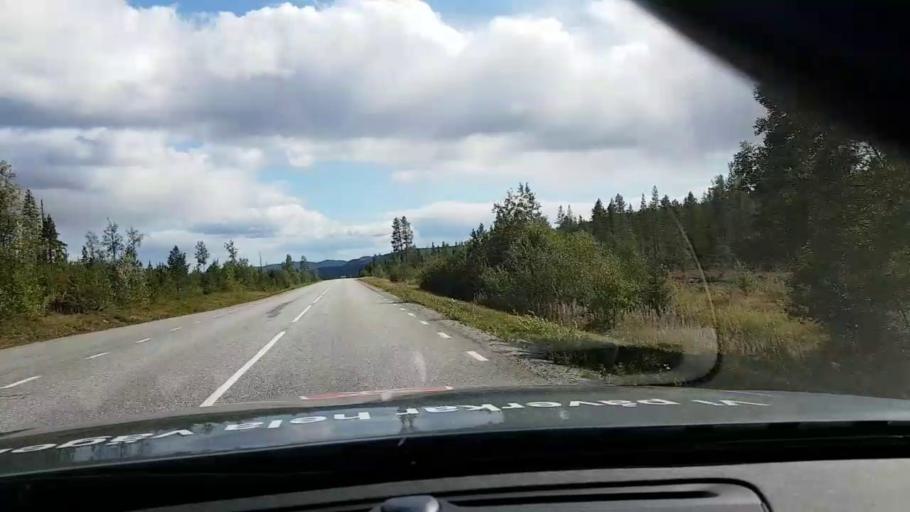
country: SE
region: Vaesterbotten
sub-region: Asele Kommun
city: Asele
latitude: 63.7703
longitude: 17.6809
